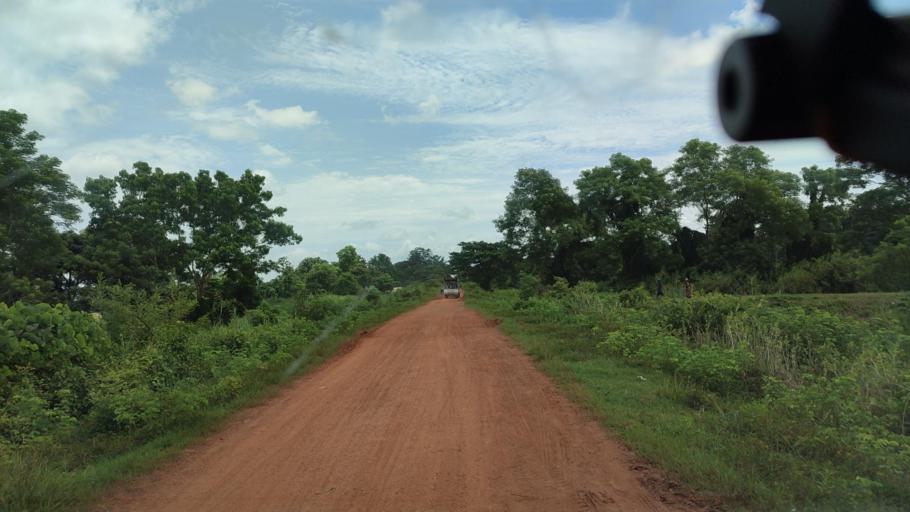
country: MM
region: Bago
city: Letpandan
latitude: 17.7429
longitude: 95.6015
